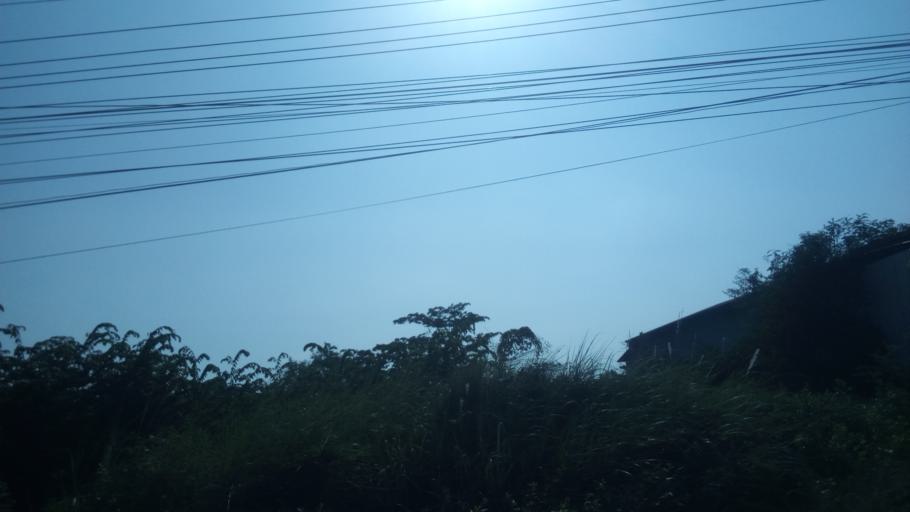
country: TH
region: Nonthaburi
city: Bang Yai
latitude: 13.8843
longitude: 100.3267
